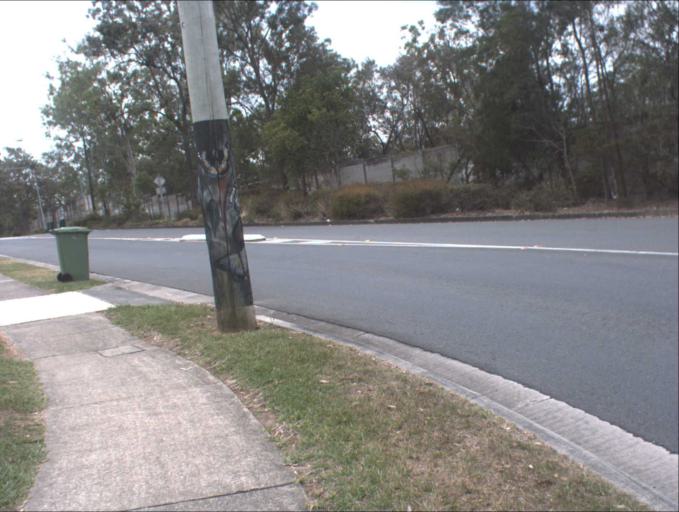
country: AU
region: Queensland
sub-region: Logan
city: Slacks Creek
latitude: -27.6738
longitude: 153.1816
